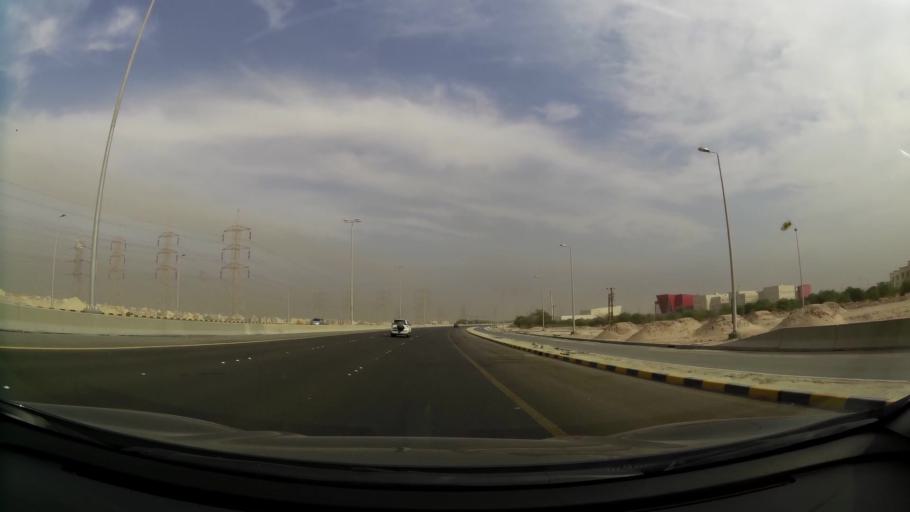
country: KW
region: Muhafazat al Jahra'
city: Al Jahra'
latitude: 29.3211
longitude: 47.7853
